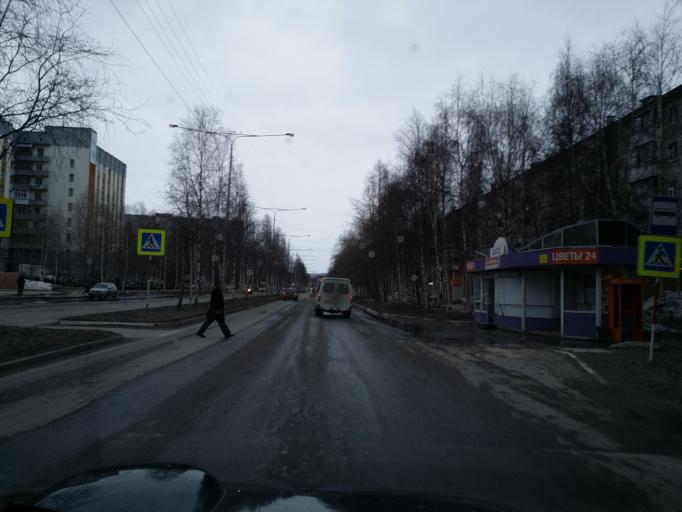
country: RU
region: Khanty-Mansiyskiy Avtonomnyy Okrug
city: Nizhnevartovsk
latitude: 60.9433
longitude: 76.5664
